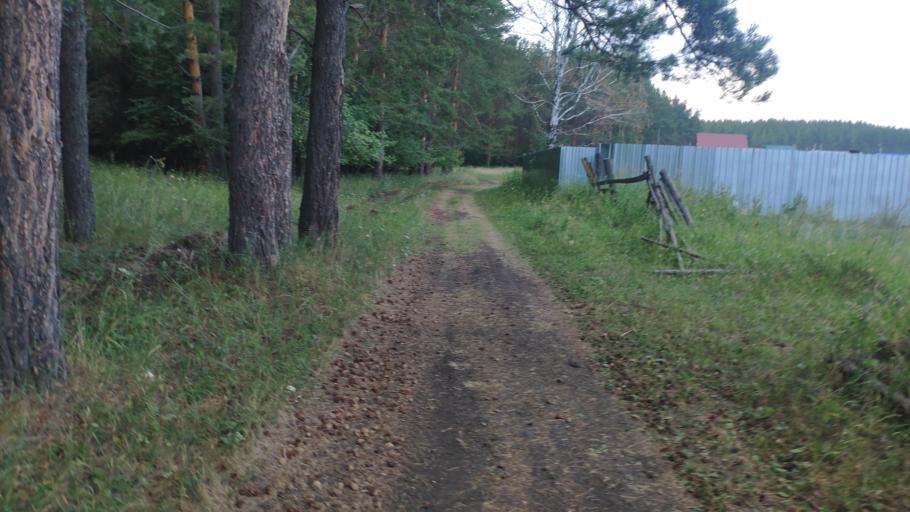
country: RU
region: Bashkortostan
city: Abzakovo
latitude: 53.8078
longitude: 58.6413
